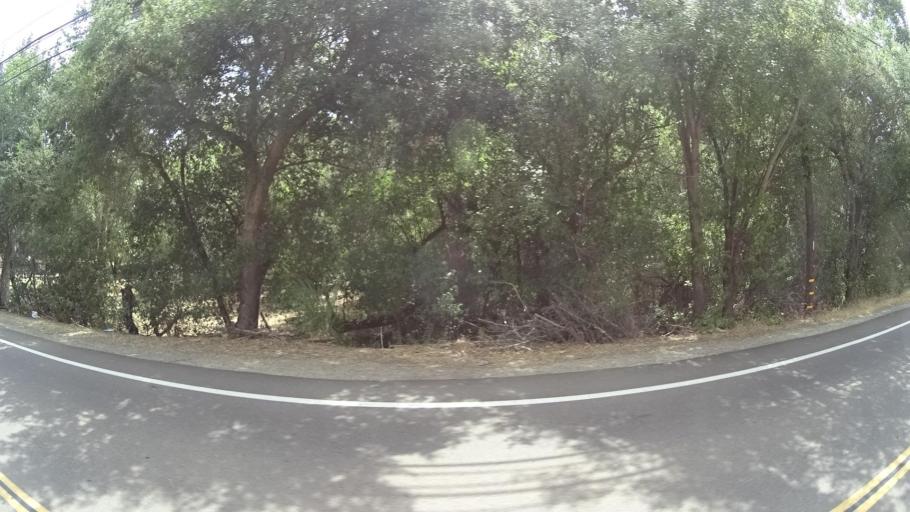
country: US
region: California
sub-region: San Diego County
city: Escondido
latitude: 33.1709
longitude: -117.1016
